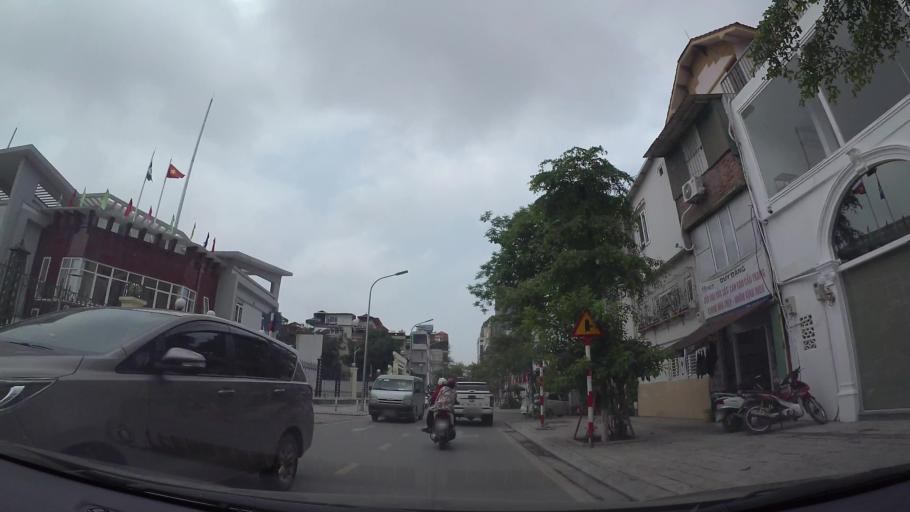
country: VN
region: Ha Noi
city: Hai BaTrung
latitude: 21.0124
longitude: 105.8463
